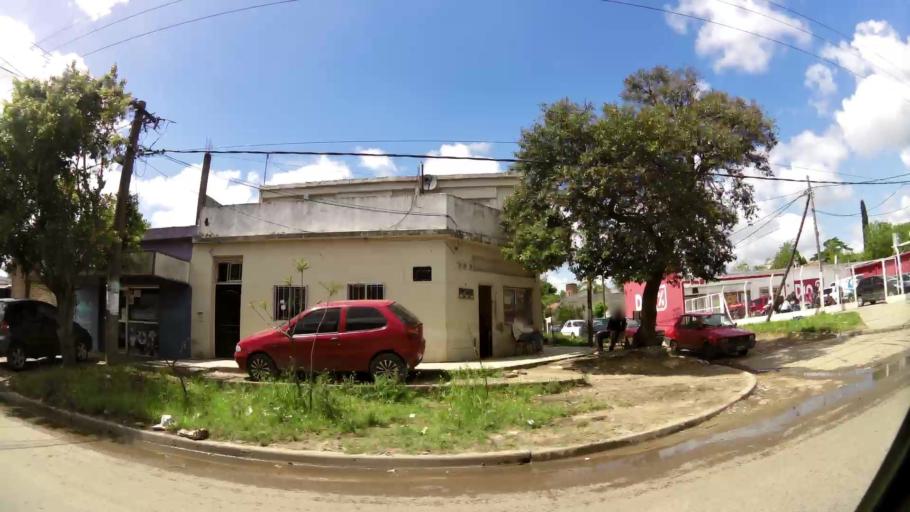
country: AR
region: Buenos Aires
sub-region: Partido de Quilmes
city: Quilmes
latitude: -34.8291
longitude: -58.2287
